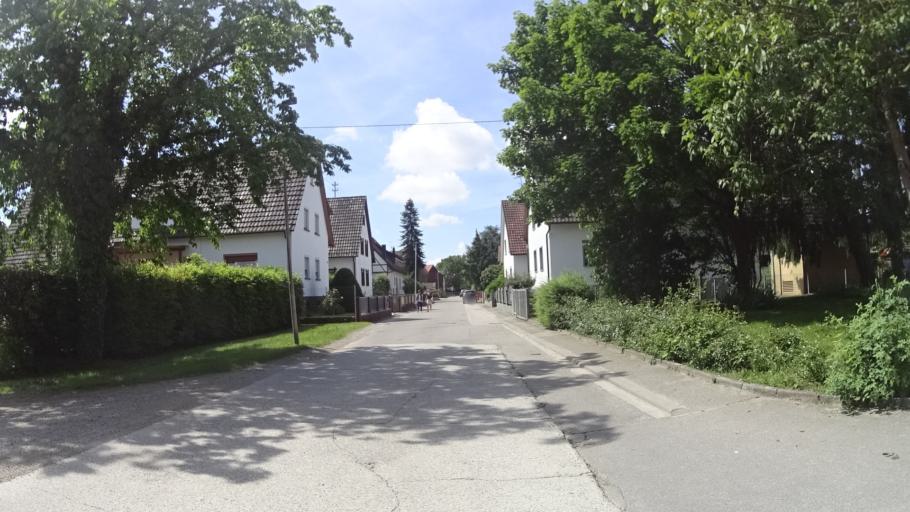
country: DE
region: Baden-Wuerttemberg
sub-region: Freiburg Region
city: Meissenheim
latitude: 48.4145
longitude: 7.7767
